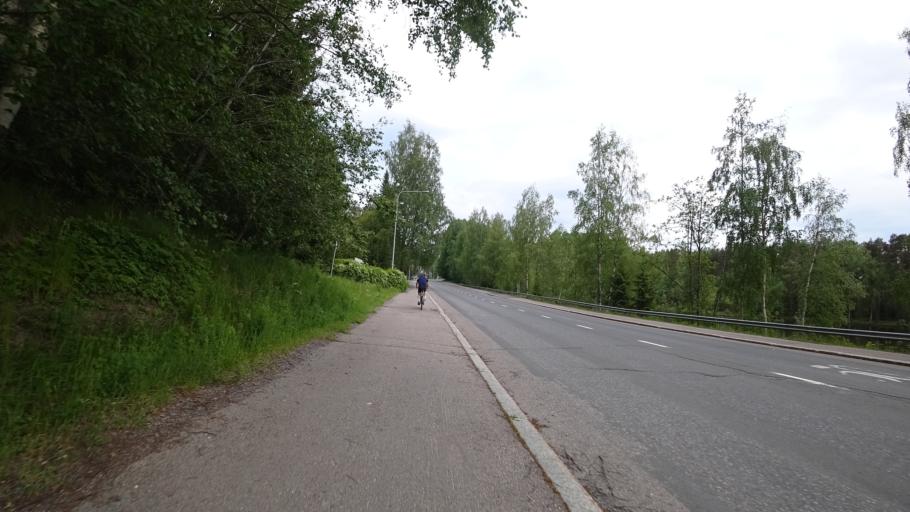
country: FI
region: Pirkanmaa
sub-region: Tampere
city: Pirkkala
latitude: 61.5186
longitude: 23.6450
